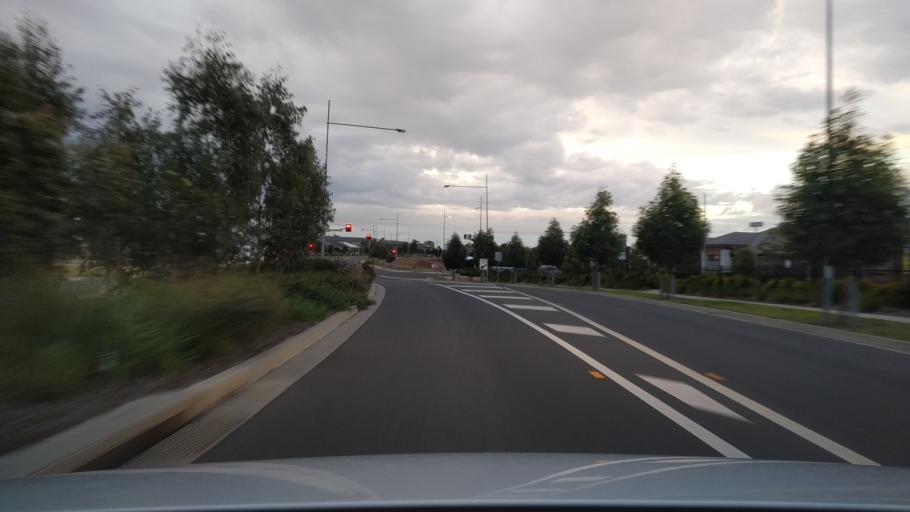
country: AU
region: New South Wales
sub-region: Camden
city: Narellan
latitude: -34.0026
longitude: 150.7356
